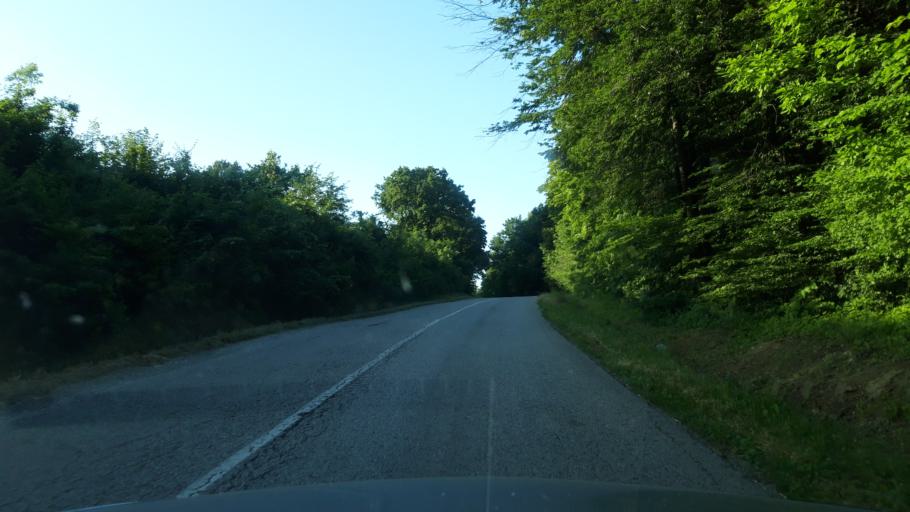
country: RS
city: Glozan
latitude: 45.1471
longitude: 19.5790
